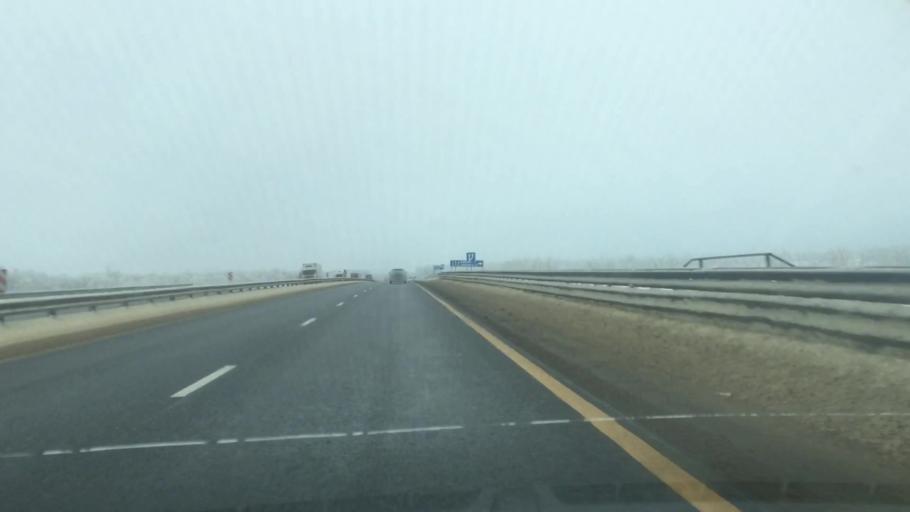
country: RU
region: Lipetsk
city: Zadonsk
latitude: 52.5044
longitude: 38.7555
